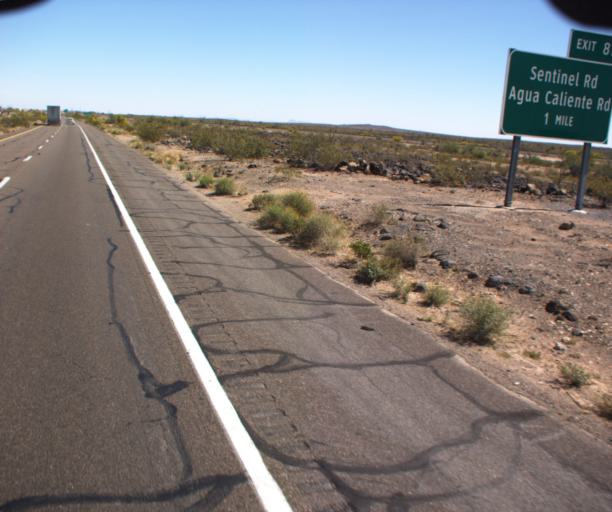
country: US
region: Arizona
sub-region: Maricopa County
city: Gila Bend
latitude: 32.8563
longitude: -113.2345
